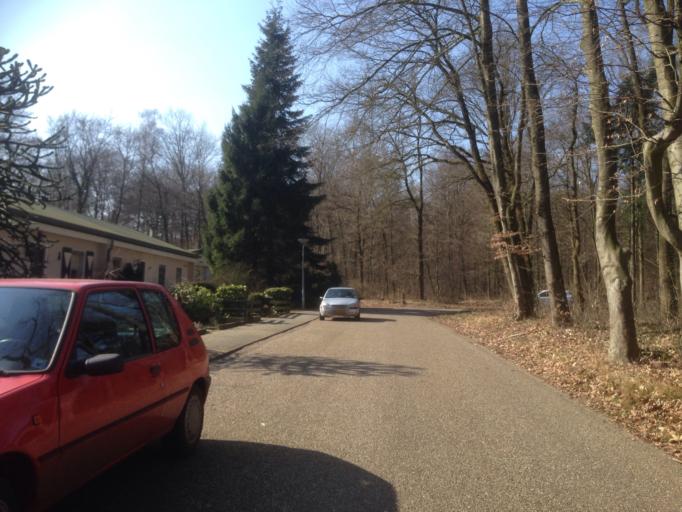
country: NL
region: Gelderland
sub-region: Gemeente Overbetuwe
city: Randwijk
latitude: 51.9664
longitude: 5.7024
